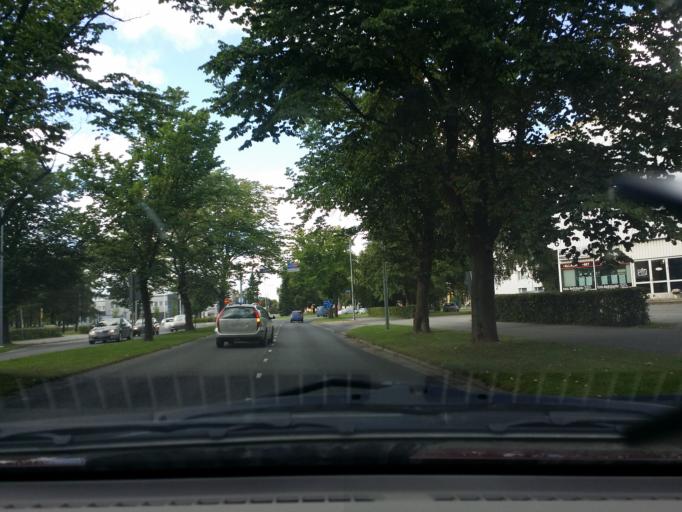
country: FI
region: Satakunta
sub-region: Pori
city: Pori
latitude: 61.4798
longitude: 21.7870
